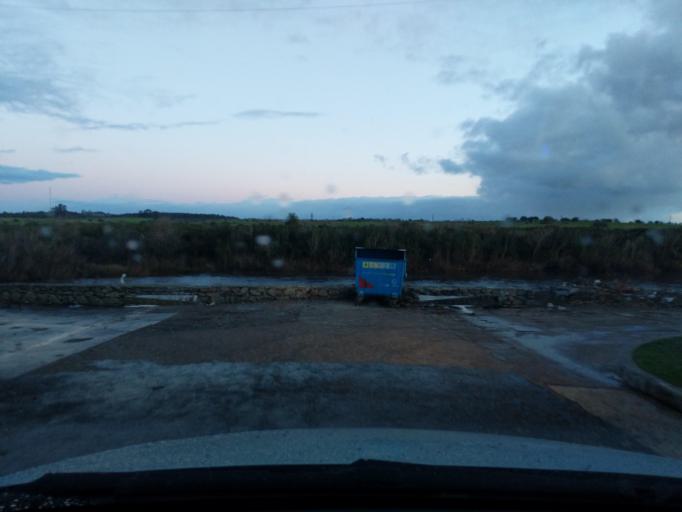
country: UY
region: Florida
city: Florida
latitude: -34.1102
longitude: -56.2099
